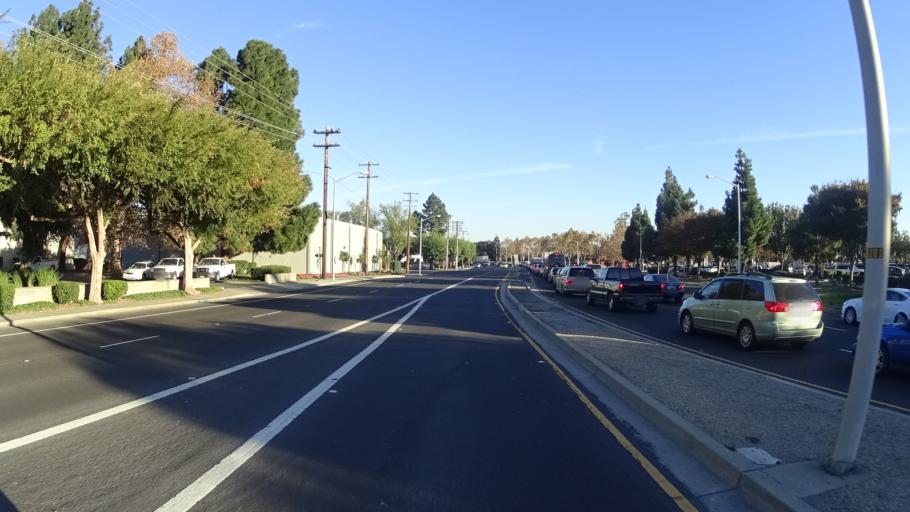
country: US
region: California
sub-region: Santa Clara County
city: Santa Clara
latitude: 37.3582
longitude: -121.9383
